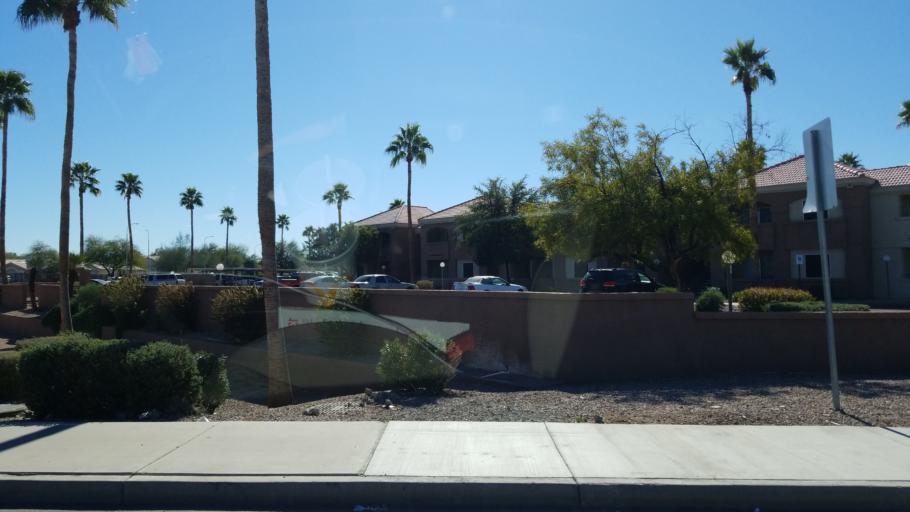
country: US
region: Arizona
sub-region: Maricopa County
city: Chandler
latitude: 33.3206
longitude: -111.8334
